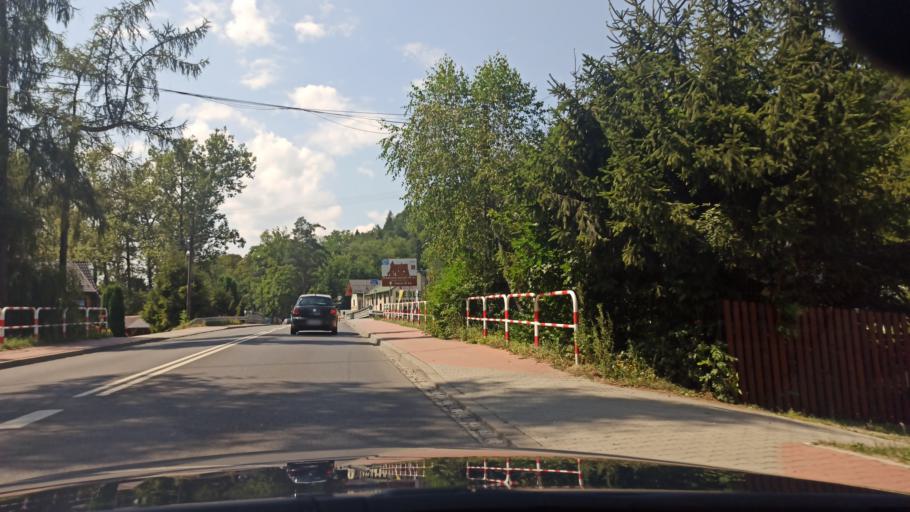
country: PL
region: Lesser Poland Voivodeship
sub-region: Powiat nowotarski
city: Kroscienko nad Dunajcem
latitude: 49.4407
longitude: 20.4185
